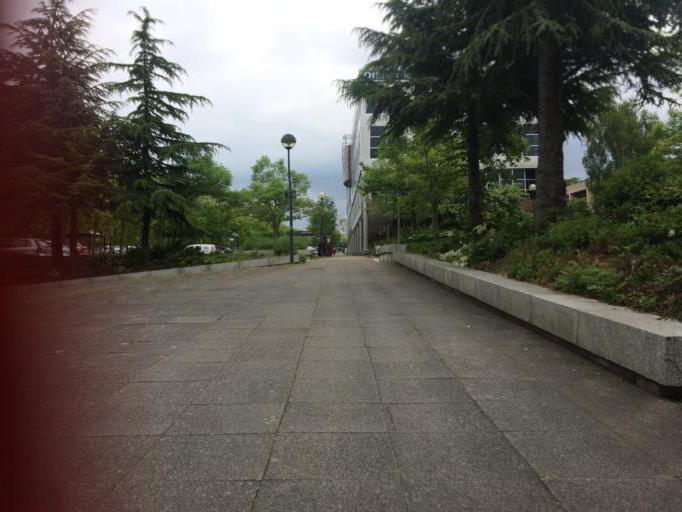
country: GB
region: England
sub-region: Milton Keynes
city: Milton Keynes
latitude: 52.0398
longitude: -0.7663
